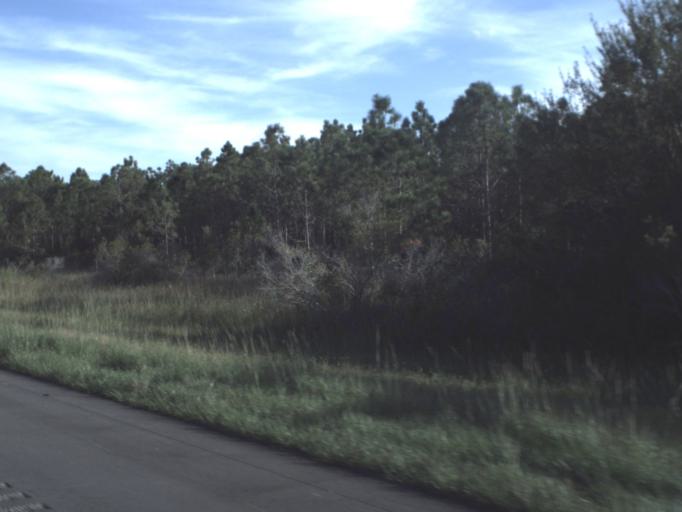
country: US
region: Florida
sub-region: Lee County
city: Suncoast Estates
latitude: 26.7981
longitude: -81.9147
